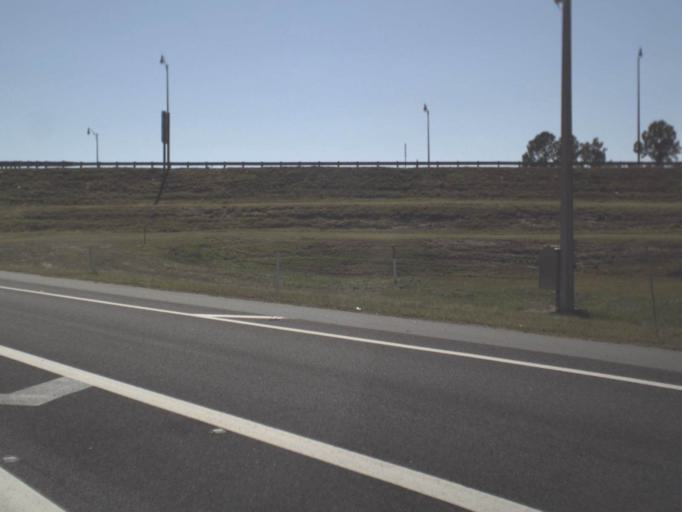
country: US
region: Florida
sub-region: Lake County
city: Hawthorne
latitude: 28.7560
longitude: -81.9396
